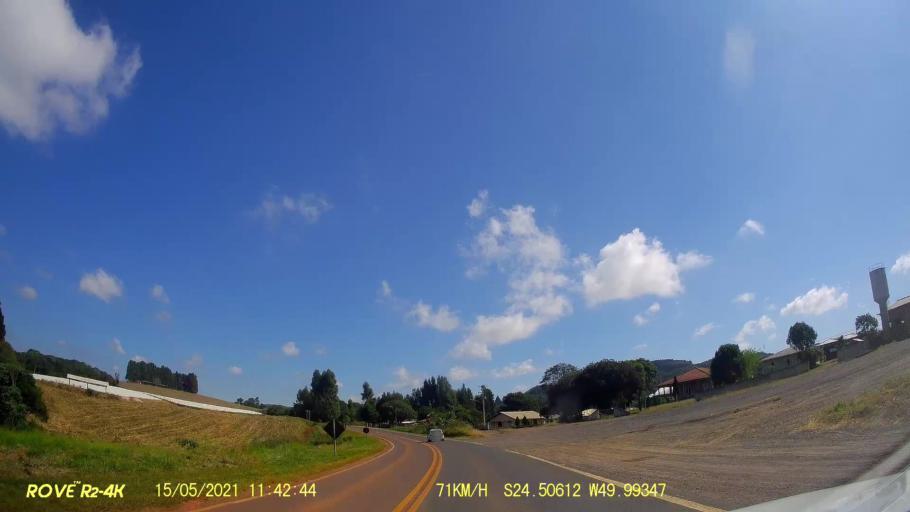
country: BR
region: Parana
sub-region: Pirai Do Sul
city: Pirai do Sul
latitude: -24.5049
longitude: -49.9931
